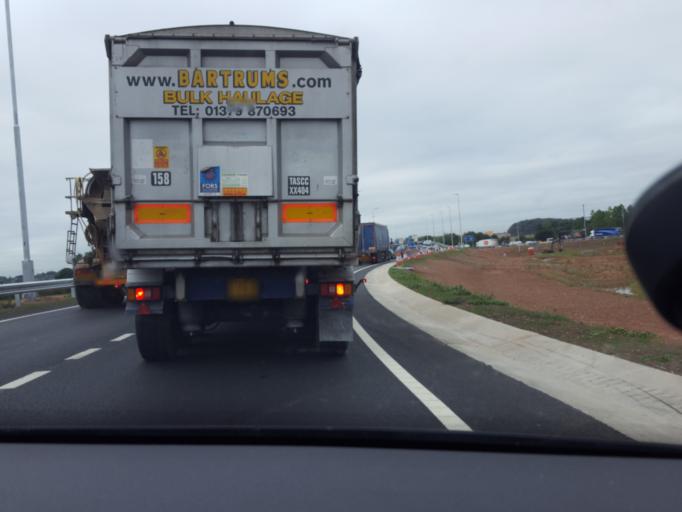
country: GB
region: England
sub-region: Leicestershire
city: Kegworth
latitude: 52.8537
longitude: -1.2948
